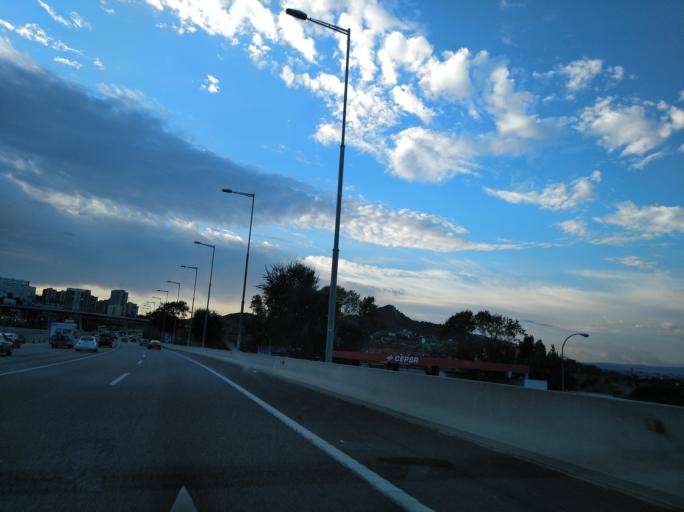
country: ES
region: Catalonia
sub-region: Provincia de Barcelona
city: Nou Barris
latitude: 41.4577
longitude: 2.1872
